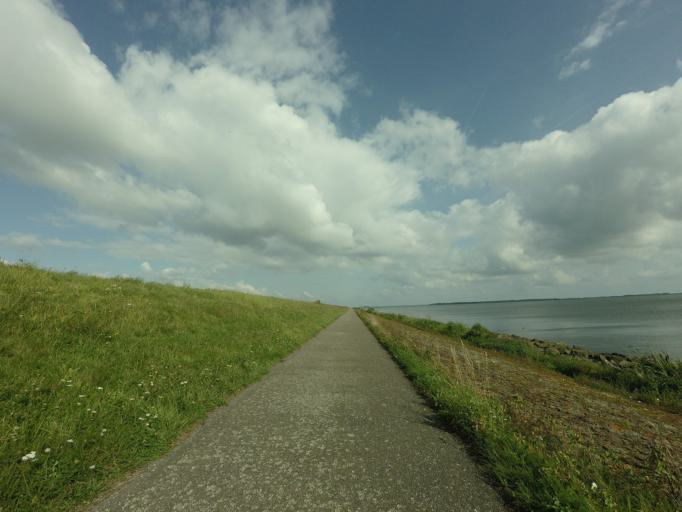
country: NL
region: Flevoland
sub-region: Gemeente Dronten
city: Dronten
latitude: 52.6131
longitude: 5.6959
